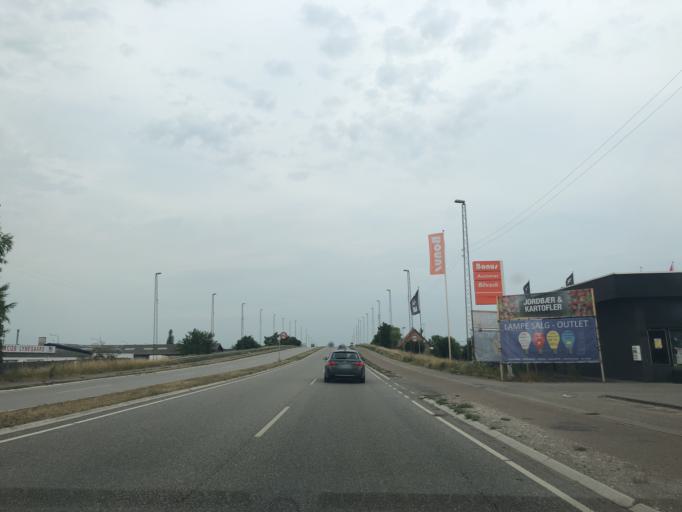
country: DK
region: Zealand
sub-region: Koge Kommune
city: Koge
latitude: 55.4713
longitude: 12.1814
